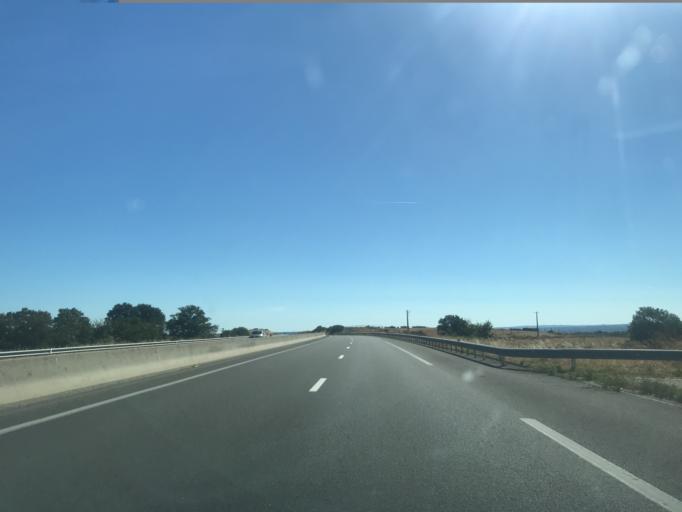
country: FR
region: Auvergne
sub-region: Departement de l'Allier
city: Quinssaines
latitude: 46.3169
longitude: 2.4971
